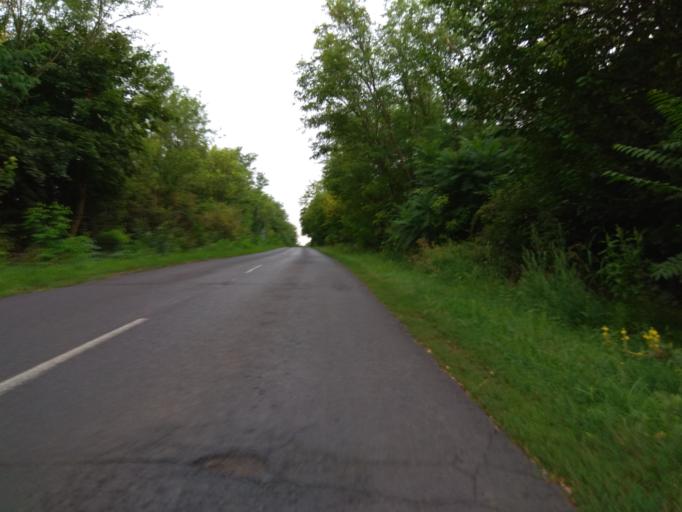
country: HU
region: Borsod-Abauj-Zemplen
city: Monok
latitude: 48.1742
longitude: 21.1130
